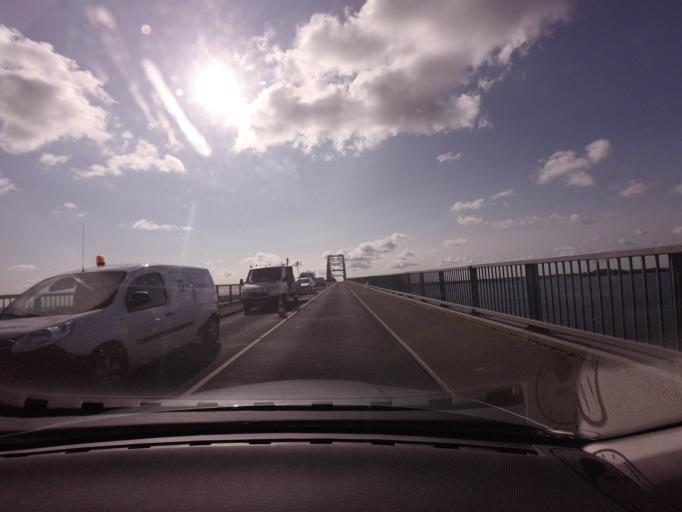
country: DK
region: Zealand
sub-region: Vordingborg Kommune
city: Stege
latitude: 54.9907
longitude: 12.1629
